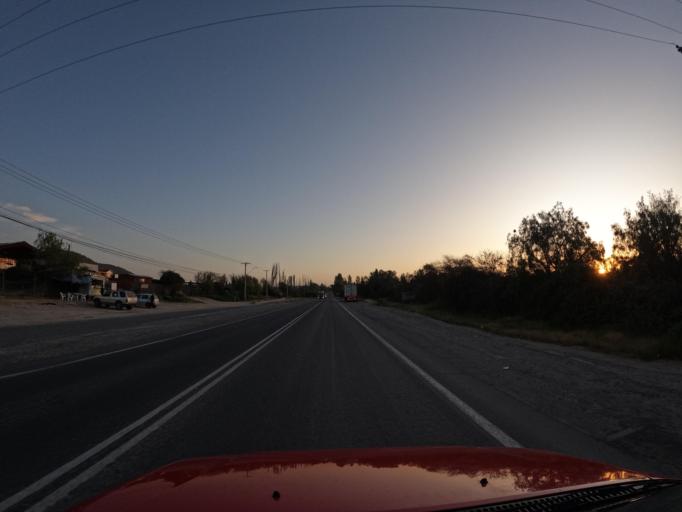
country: CL
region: O'Higgins
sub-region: Provincia de Cachapoal
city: San Vicente
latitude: -34.1611
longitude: -71.3921
